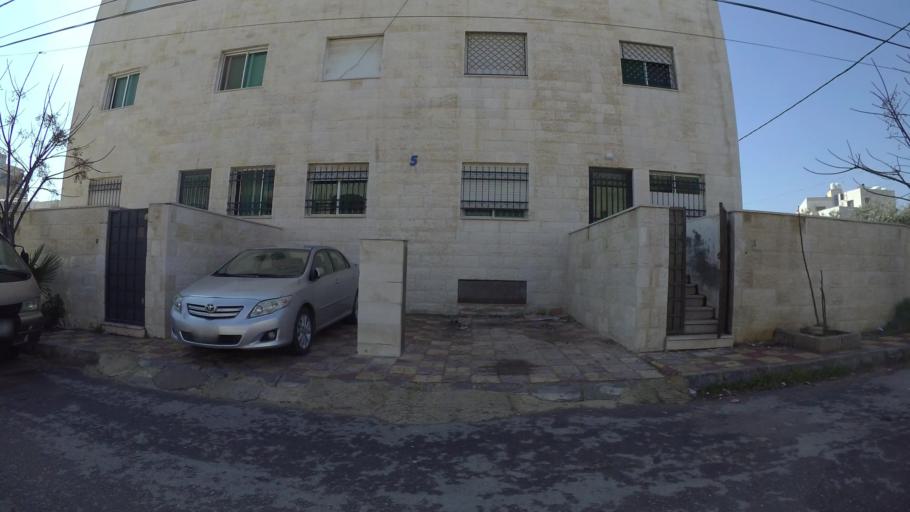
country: JO
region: Amman
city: Al Bunayyat ash Shamaliyah
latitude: 31.8946
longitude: 35.8969
